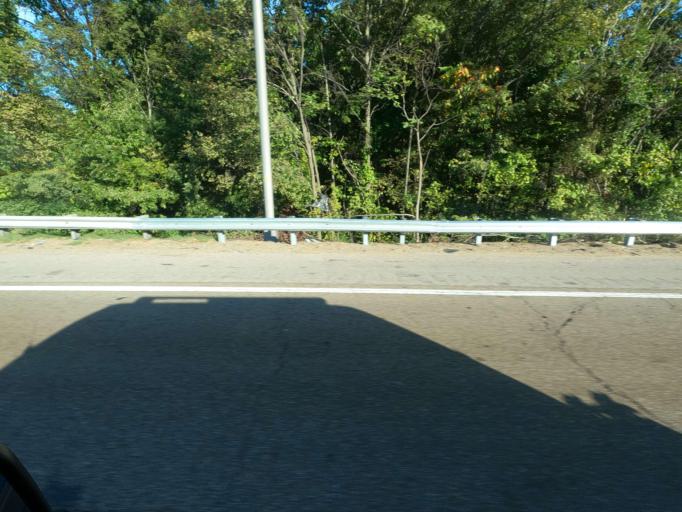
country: US
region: Tennessee
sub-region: Shelby County
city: Memphis
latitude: 35.1198
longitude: -90.0257
